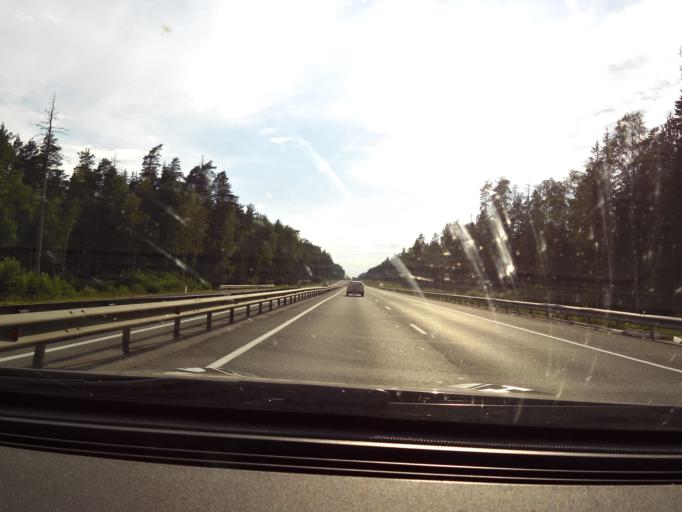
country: RU
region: Vladimir
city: Stepantsevo
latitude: 56.2259
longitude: 41.6271
